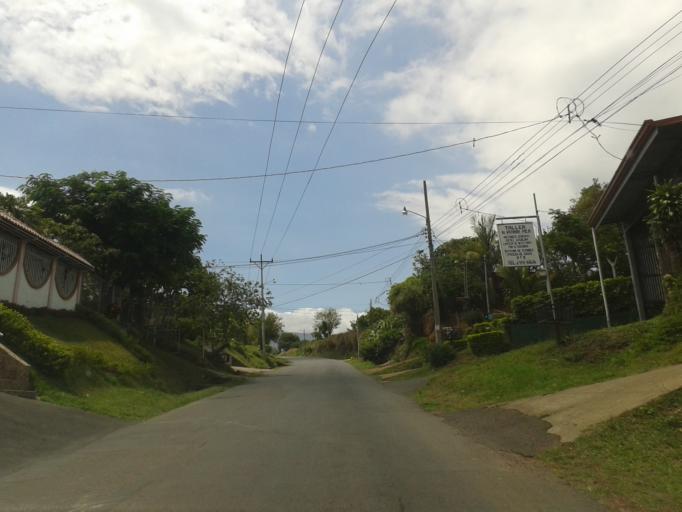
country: CR
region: Alajuela
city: Sabanilla
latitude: 10.0705
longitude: -84.1932
